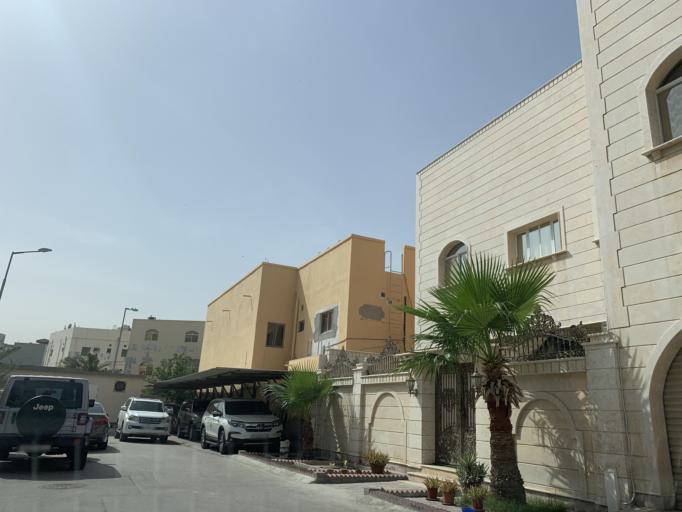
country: BH
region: Northern
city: Madinat `Isa
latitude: 26.1723
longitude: 50.5668
